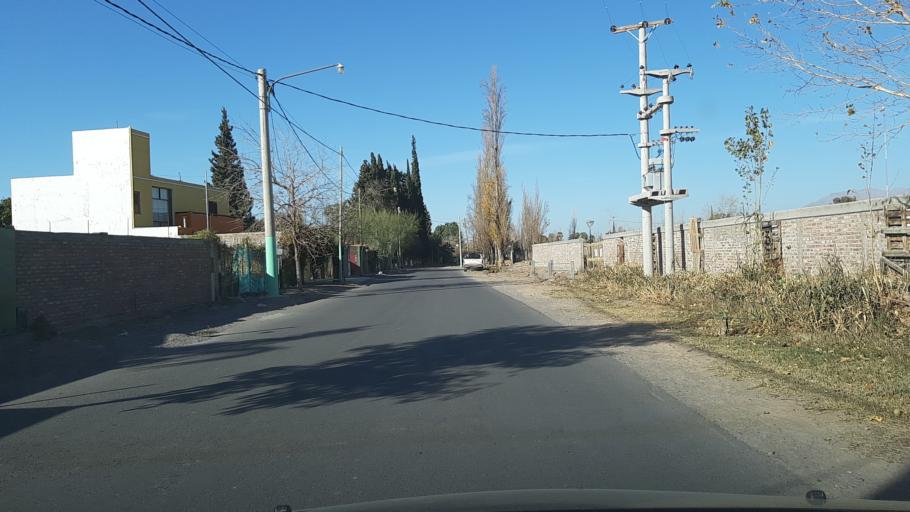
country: AR
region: San Juan
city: San Juan
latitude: -31.5256
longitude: -68.5922
